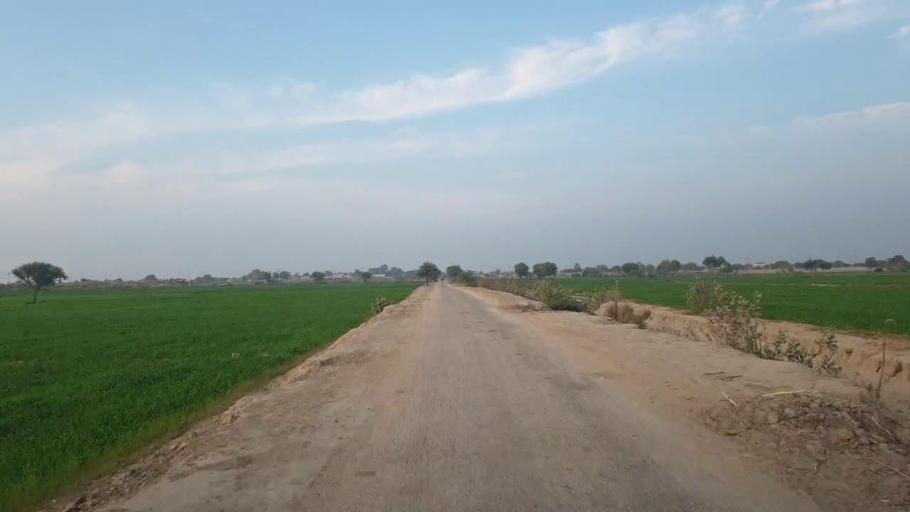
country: PK
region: Sindh
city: Shahpur Chakar
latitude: 26.1151
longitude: 68.5465
